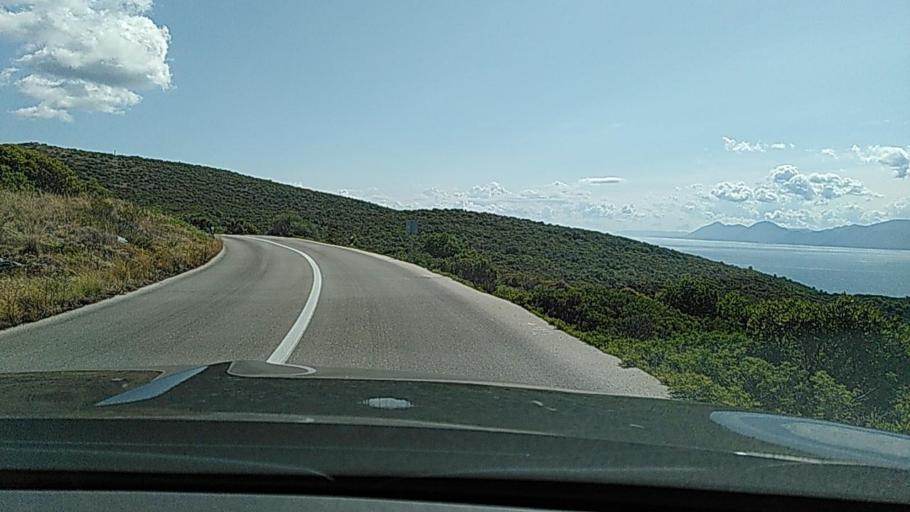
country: HR
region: Splitsko-Dalmatinska
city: Tucepi
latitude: 43.1248
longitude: 17.0999
